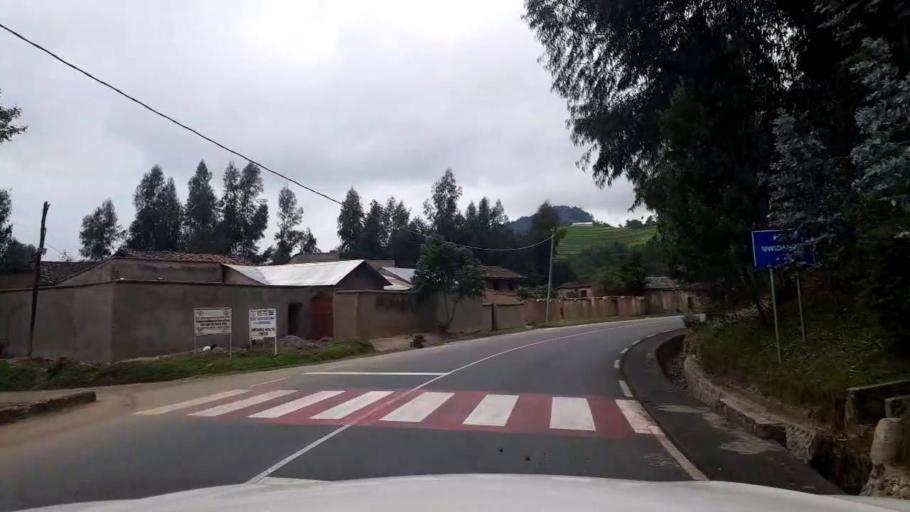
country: RW
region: Northern Province
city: Musanze
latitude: -1.6533
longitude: 29.5113
